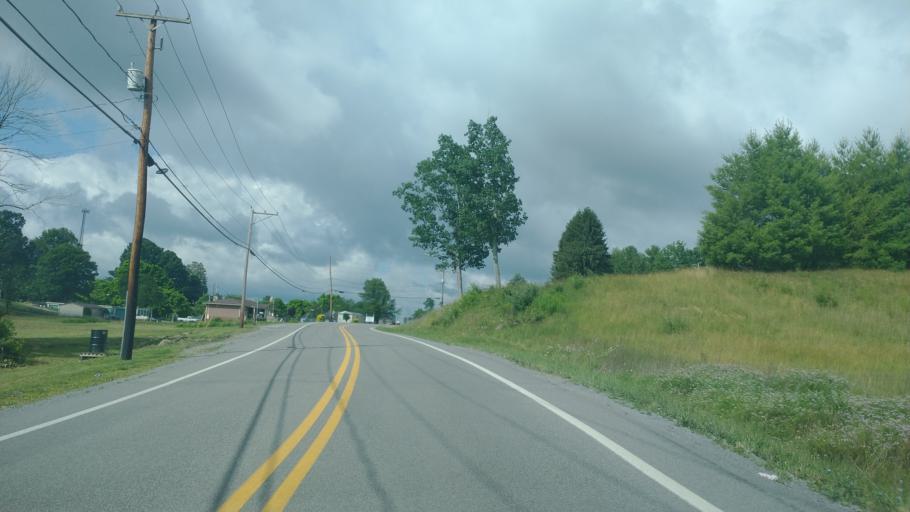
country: US
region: West Virginia
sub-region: Mercer County
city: Princeton
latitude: 37.3572
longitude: -81.1450
